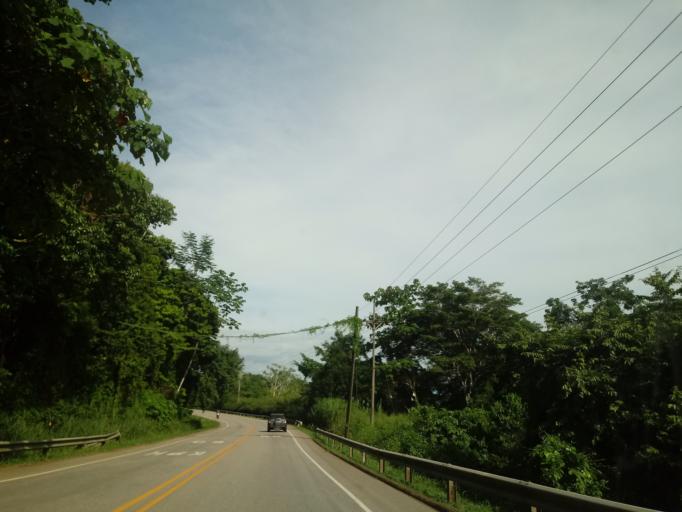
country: CR
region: San Jose
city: Daniel Flores
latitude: 9.2064
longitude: -83.8009
